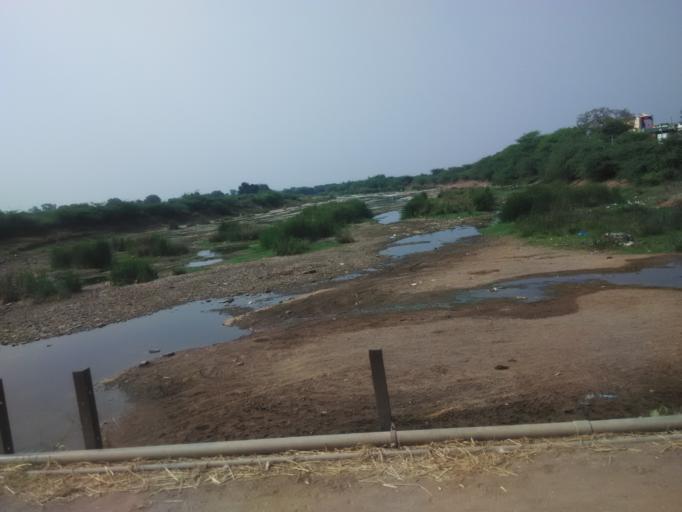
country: IN
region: Andhra Pradesh
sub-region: Kurnool
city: Nandyal
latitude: 15.4493
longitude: 78.4208
